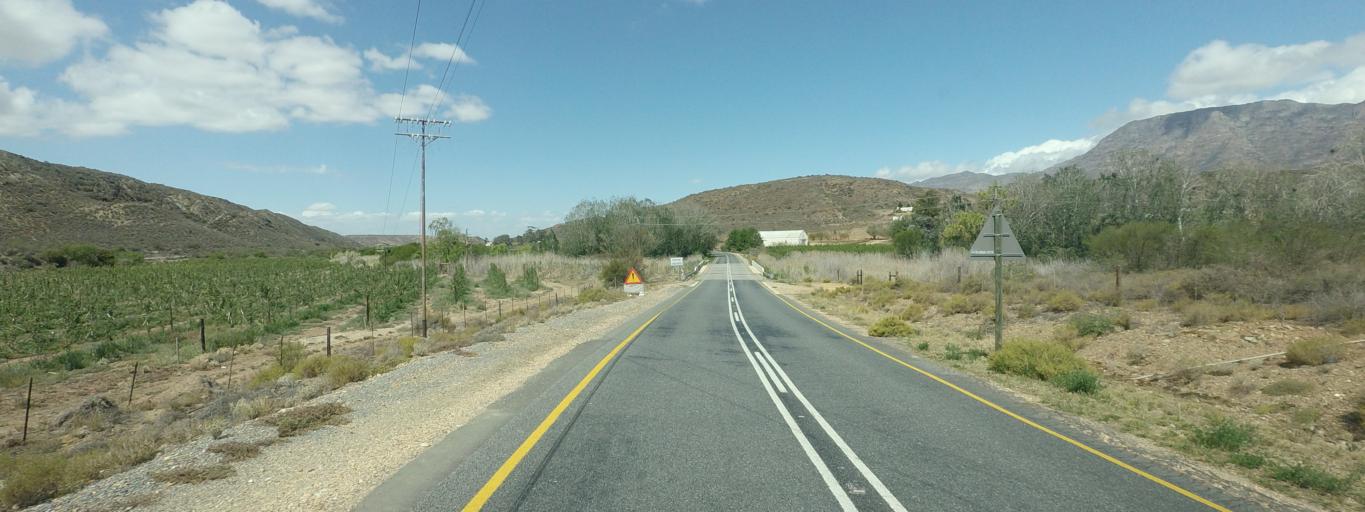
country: ZA
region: Western Cape
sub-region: Overberg District Municipality
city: Swellendam
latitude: -33.8559
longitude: 20.7976
